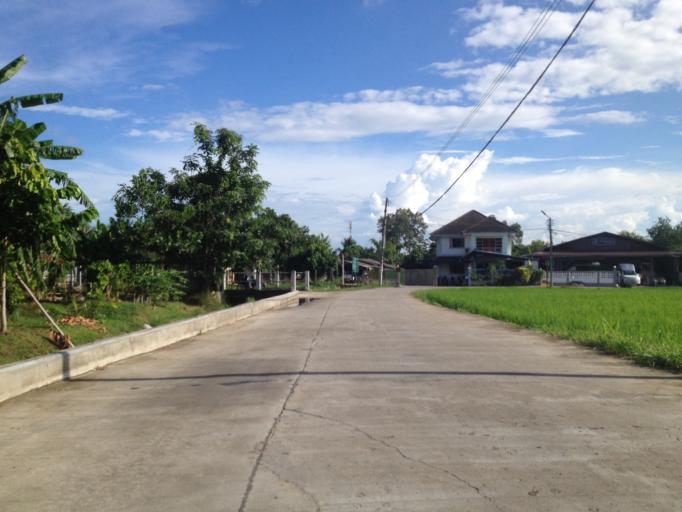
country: TH
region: Chiang Mai
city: Hang Dong
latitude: 18.6995
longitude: 98.9165
